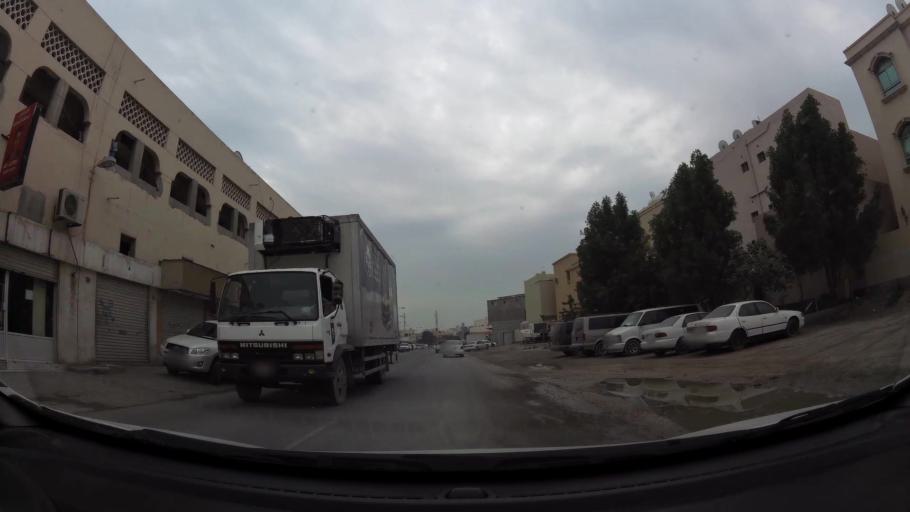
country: BH
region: Northern
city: Sitrah
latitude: 26.1675
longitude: 50.6148
